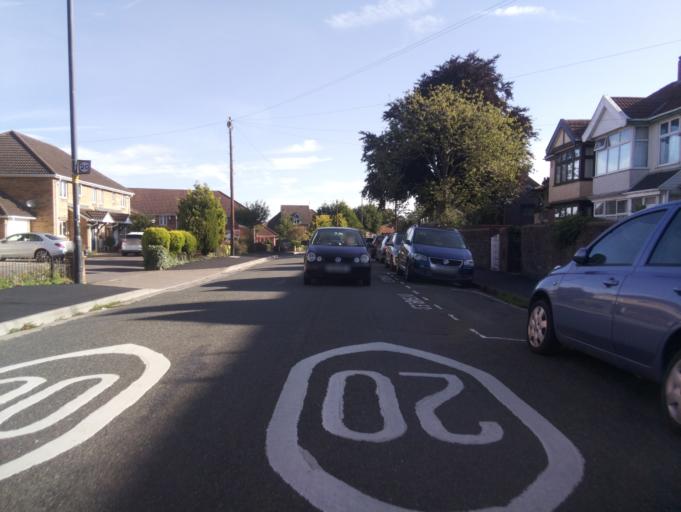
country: GB
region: England
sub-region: Bath and North East Somerset
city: Whitchurch
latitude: 51.4439
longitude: -2.5492
